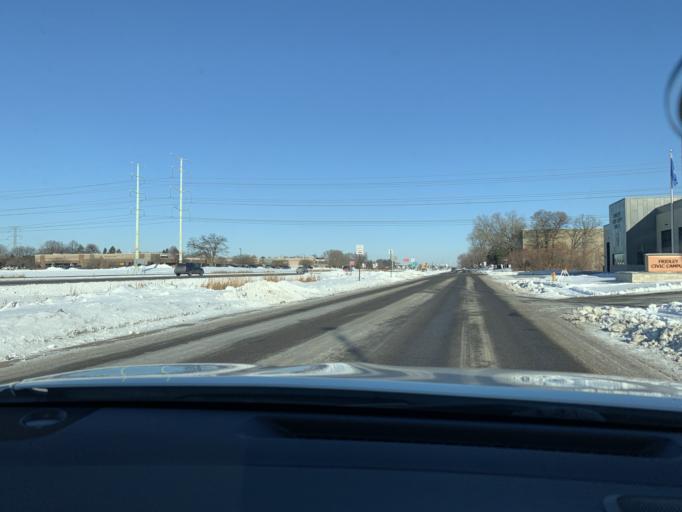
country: US
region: Minnesota
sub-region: Anoka County
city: Fridley
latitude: 45.0957
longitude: -93.2630
